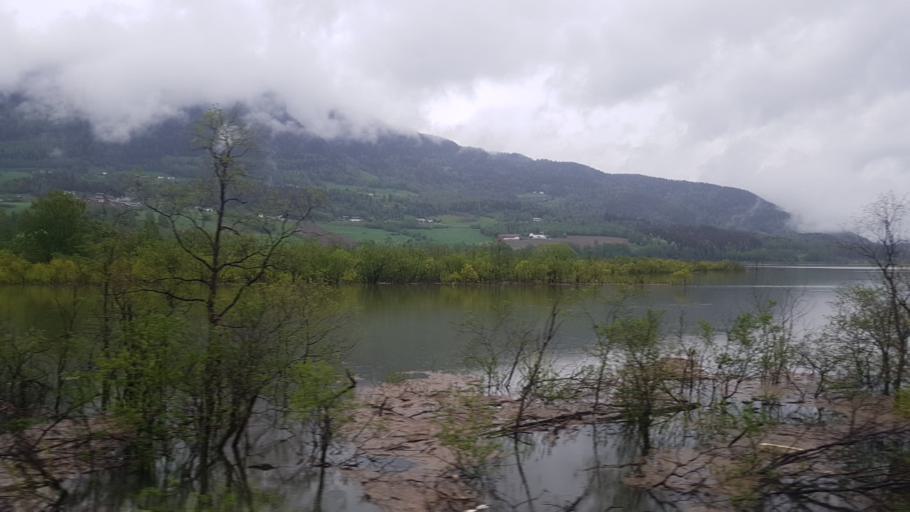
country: NO
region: Oppland
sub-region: Ringebu
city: Ringebu
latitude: 61.4481
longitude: 10.2091
